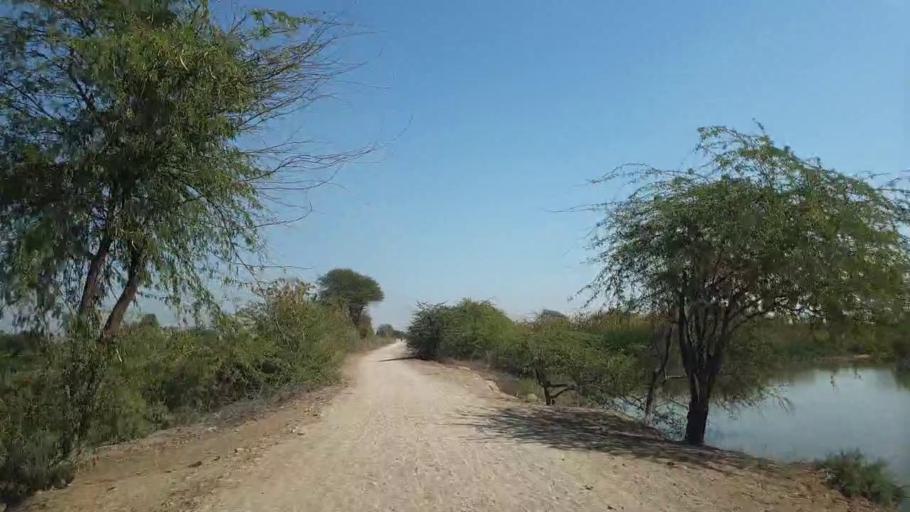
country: PK
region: Sindh
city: Mirpur Khas
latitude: 25.5922
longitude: 69.0968
